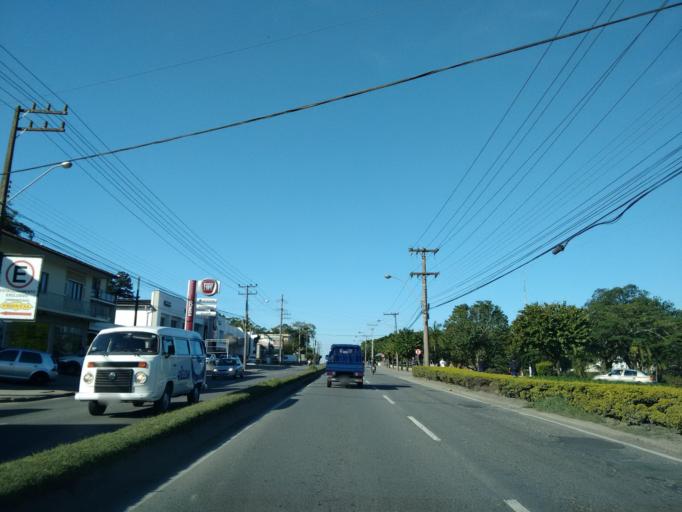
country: BR
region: Santa Catarina
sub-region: Jaragua Do Sul
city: Jaragua do Sul
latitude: -26.4782
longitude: -49.0531
